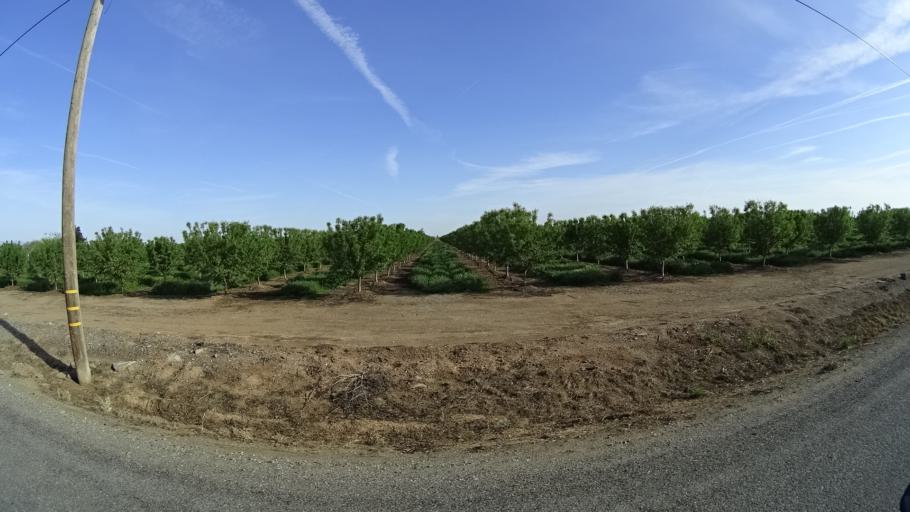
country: US
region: California
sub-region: Glenn County
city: Orland
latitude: 39.7188
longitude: -122.2300
